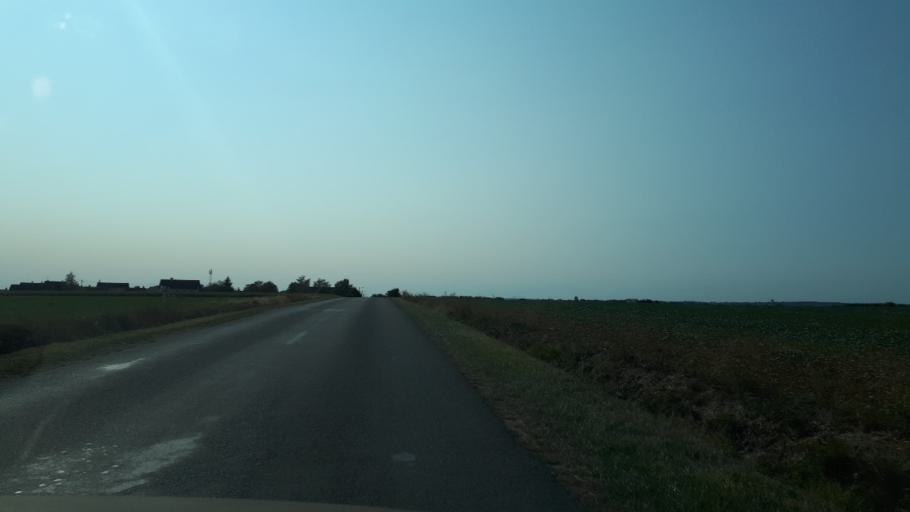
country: FR
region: Centre
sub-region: Departement du Cher
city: Rians
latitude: 47.1864
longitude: 2.6274
